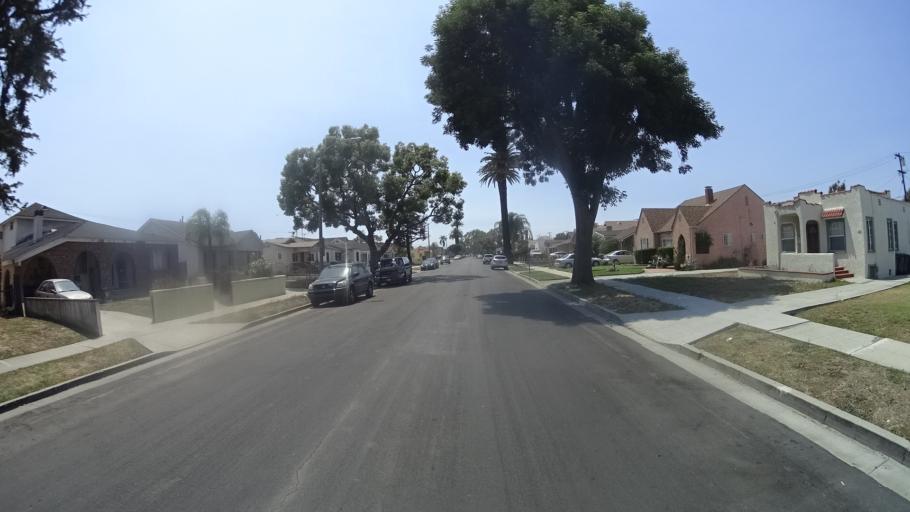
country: US
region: California
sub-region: Los Angeles County
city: Westmont
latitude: 33.9691
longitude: -118.3118
